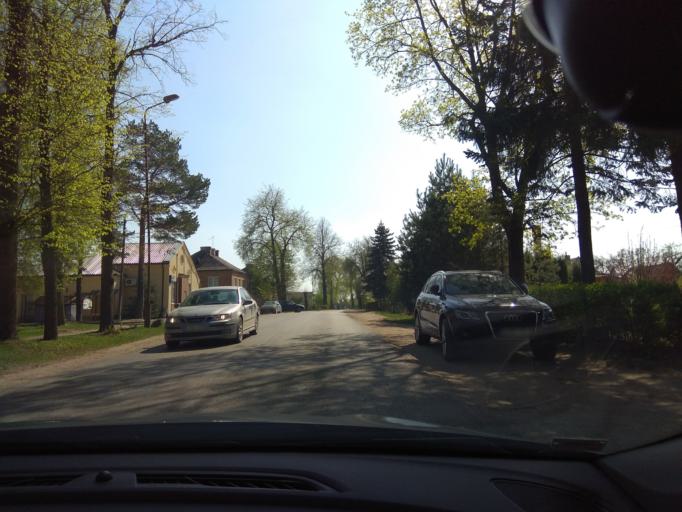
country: LT
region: Panevezys
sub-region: Panevezys City
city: Panevezys
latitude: 55.9015
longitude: 24.2376
